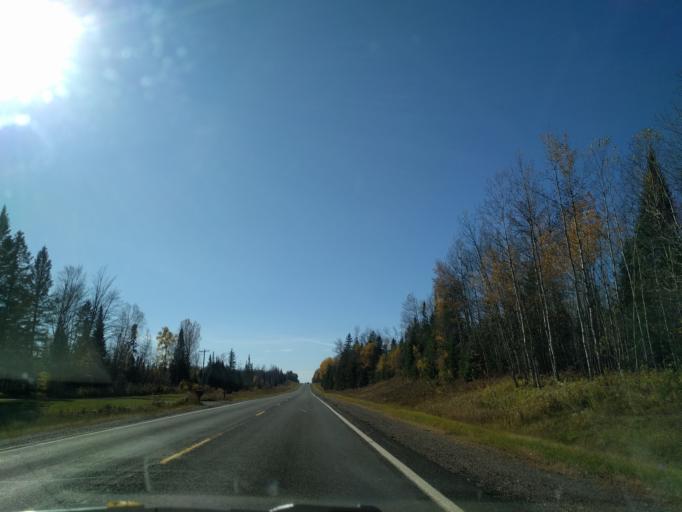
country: US
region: Michigan
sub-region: Marquette County
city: West Ishpeming
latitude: 46.3093
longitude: -87.9805
